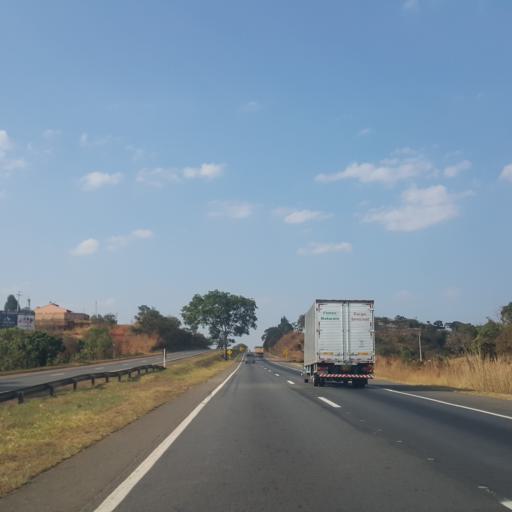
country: BR
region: Goias
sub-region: Abadiania
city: Abadiania
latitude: -16.0957
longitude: -48.5191
